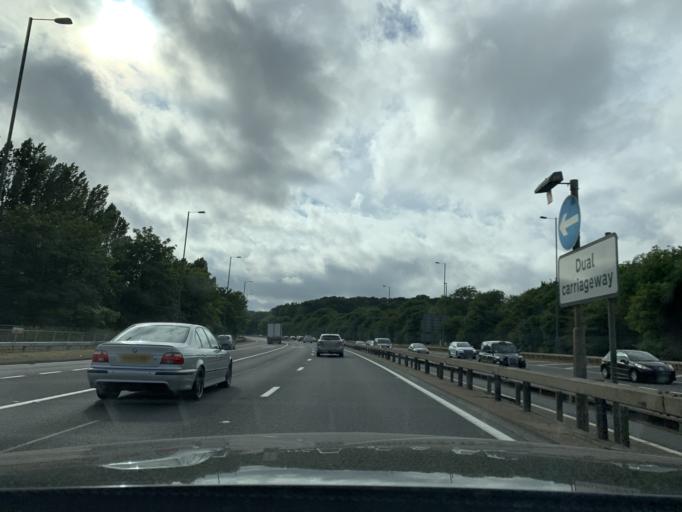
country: GB
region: England
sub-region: Greater London
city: Bexley
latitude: 51.4476
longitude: 0.1538
